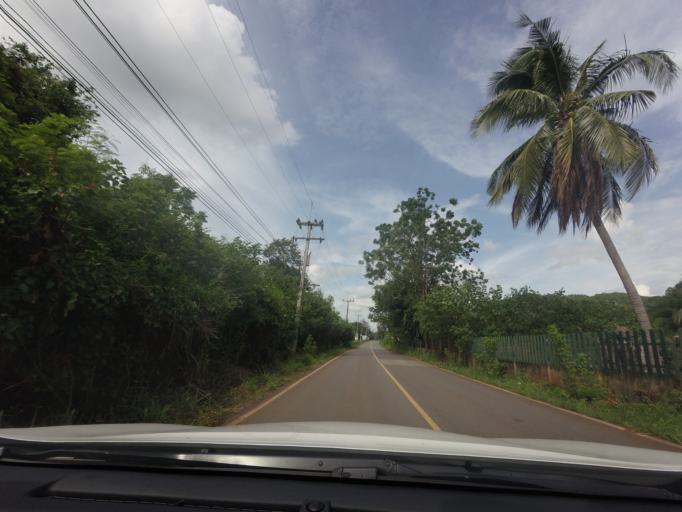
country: TH
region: Nakhon Ratchasima
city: Pak Chong
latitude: 14.5442
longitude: 101.4100
